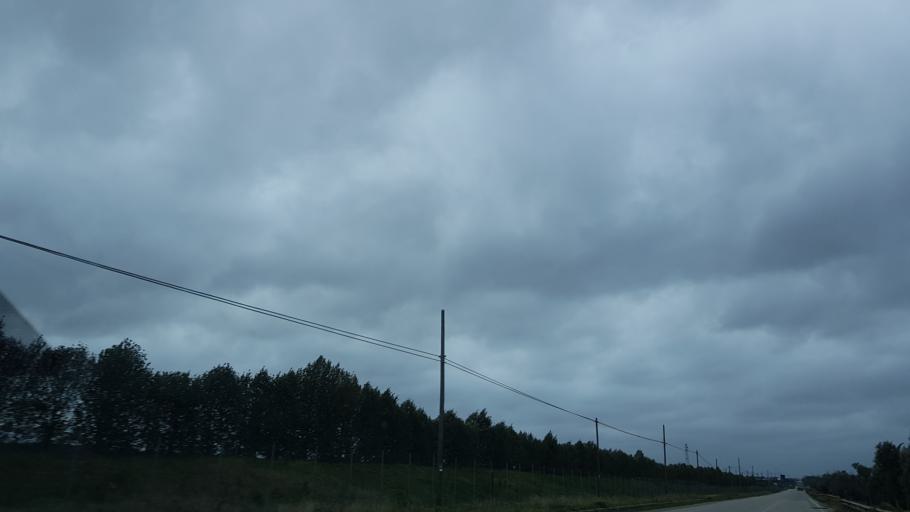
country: IT
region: Apulia
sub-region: Provincia di Brindisi
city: San Vito dei Normanni
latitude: 40.6527
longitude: 17.7966
